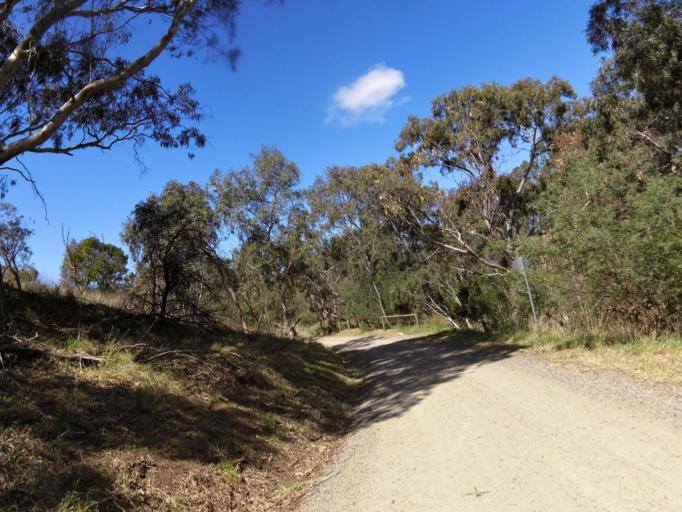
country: AU
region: Victoria
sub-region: Brimbank
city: Albion
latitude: -37.7509
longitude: 144.8486
